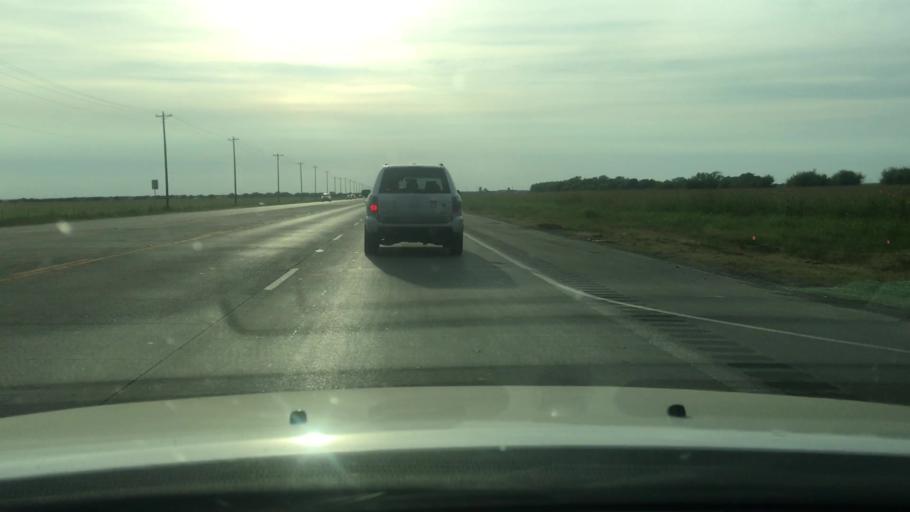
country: US
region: Texas
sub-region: Collin County
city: Prosper
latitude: 33.2195
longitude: -96.8455
